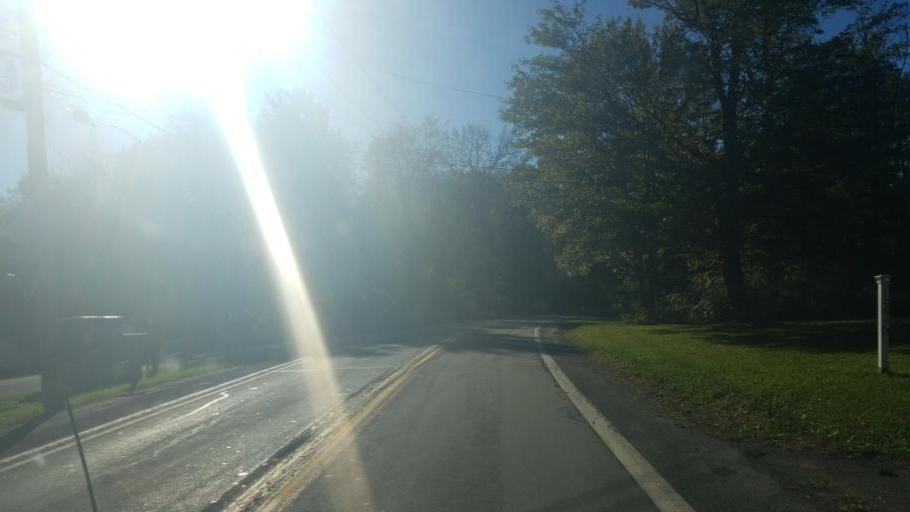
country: US
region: Pennsylvania
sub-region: Beaver County
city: Midland
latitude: 40.5530
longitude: -80.4295
